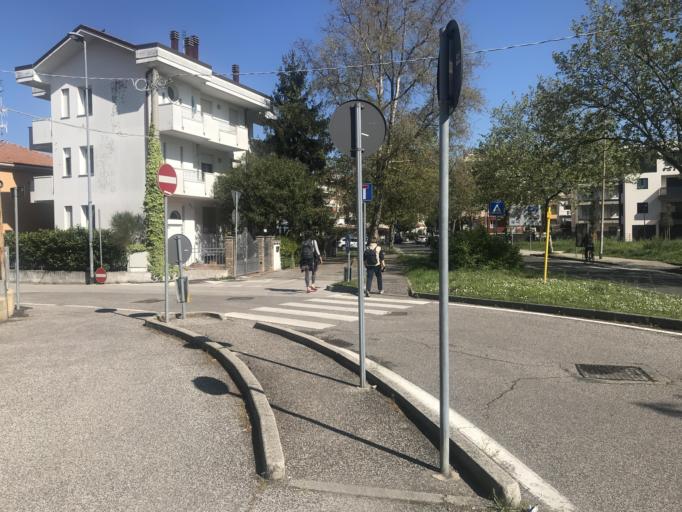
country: IT
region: Emilia-Romagna
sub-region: Provincia di Rimini
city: Rimini
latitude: 44.0510
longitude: 12.5839
